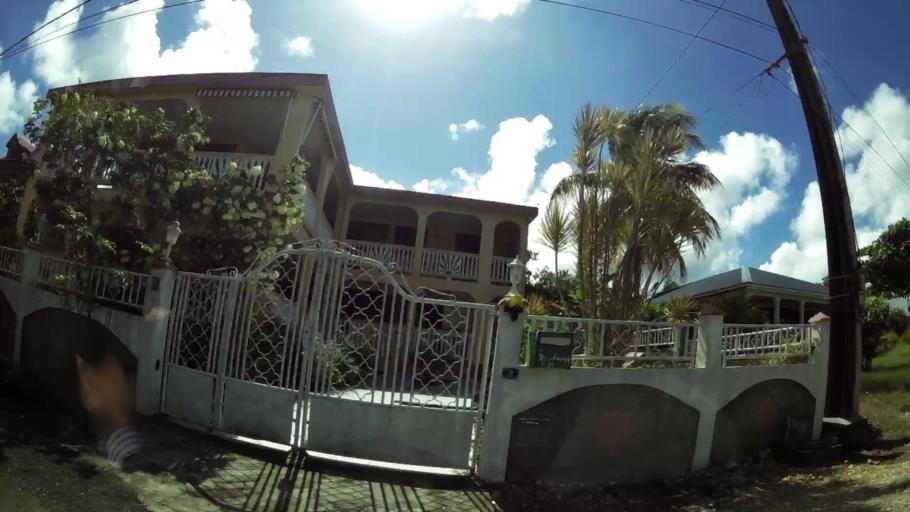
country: GP
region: Guadeloupe
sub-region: Guadeloupe
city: Anse-Bertrand
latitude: 16.4686
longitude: -61.4998
